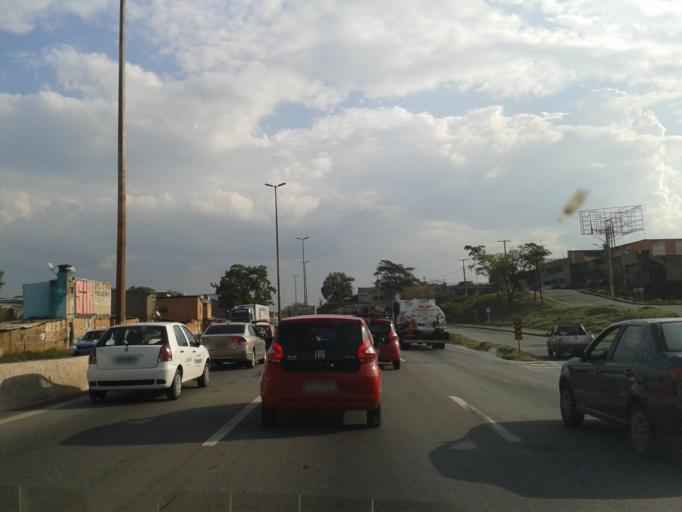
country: BR
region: Minas Gerais
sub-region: Belo Horizonte
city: Belo Horizonte
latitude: -19.8720
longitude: -43.9485
